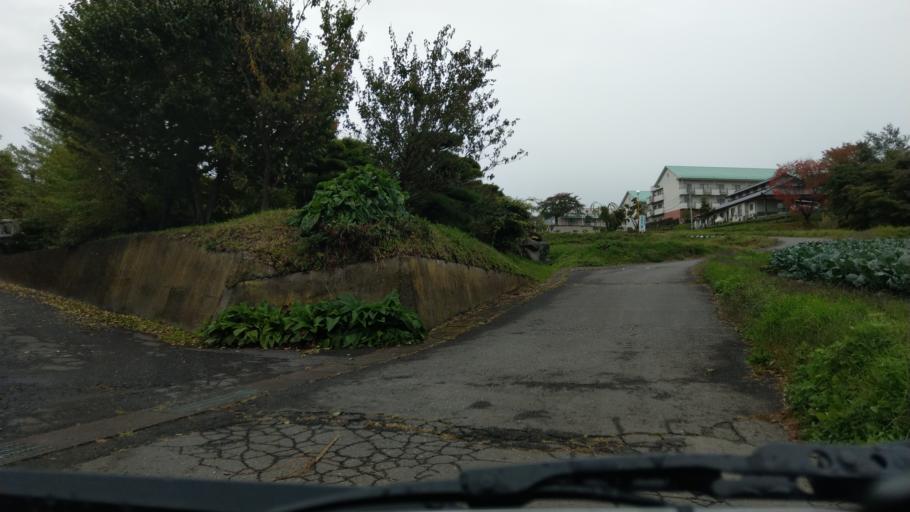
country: JP
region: Nagano
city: Komoro
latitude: 36.3365
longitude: 138.4525
